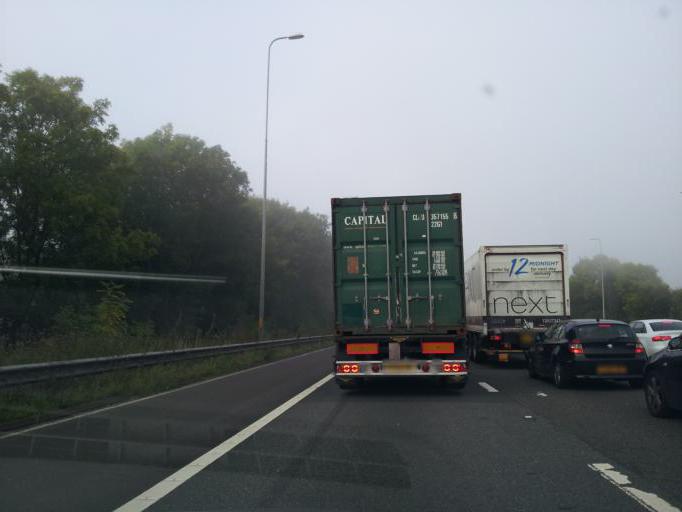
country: GB
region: England
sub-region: Borough of Rochdale
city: Rochdale
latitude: 53.5919
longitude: -2.1384
